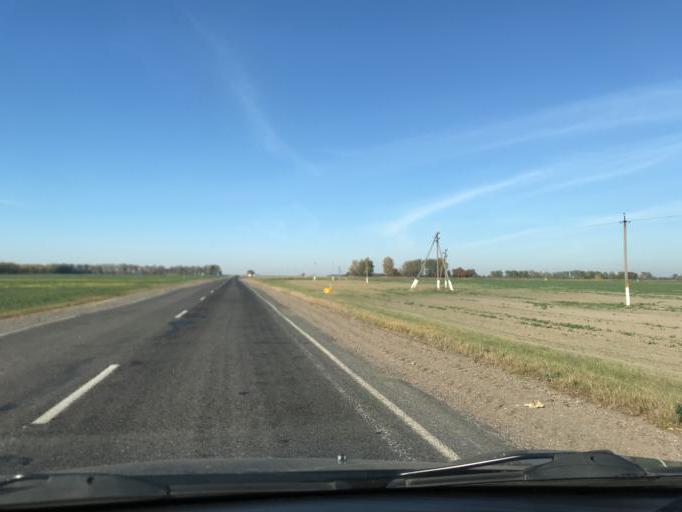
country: BY
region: Gomel
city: Brahin
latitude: 51.7958
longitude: 30.1515
